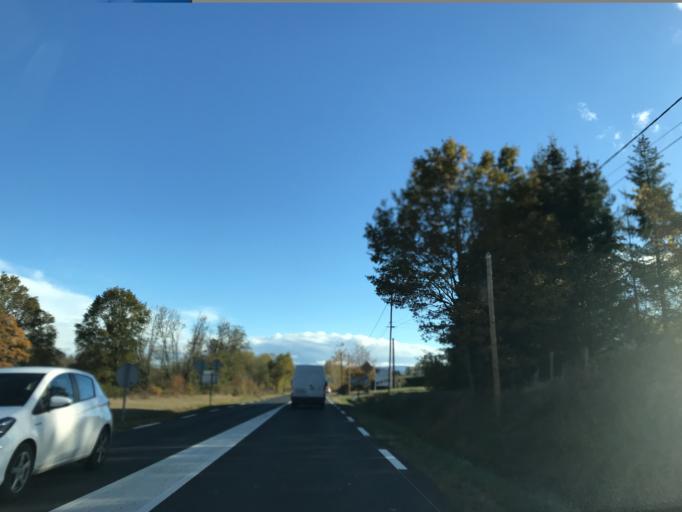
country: FR
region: Auvergne
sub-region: Departement du Puy-de-Dome
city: Peschadoires
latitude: 45.7929
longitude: 3.5251
